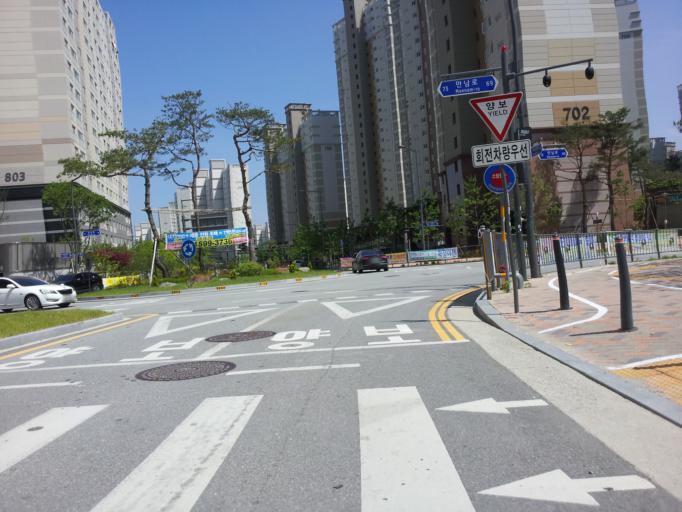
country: KR
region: Chungcheongnam-do
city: Gongju
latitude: 36.5059
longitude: 127.2383
